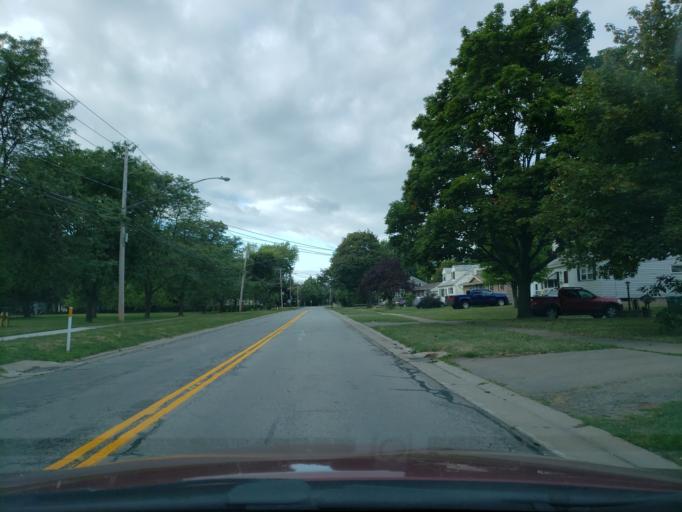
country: US
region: New York
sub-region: Monroe County
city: Greece
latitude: 43.2129
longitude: -77.6516
